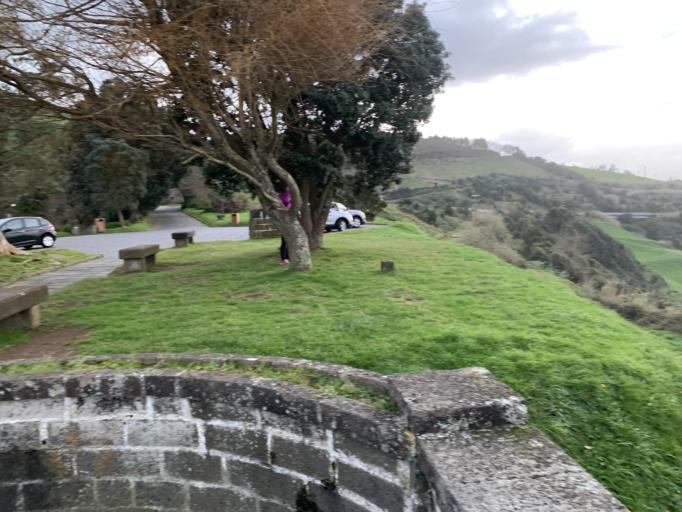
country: PT
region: Azores
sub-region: Vila Franca do Campo
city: Vila Franca do Campo
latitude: 37.8241
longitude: -25.4623
